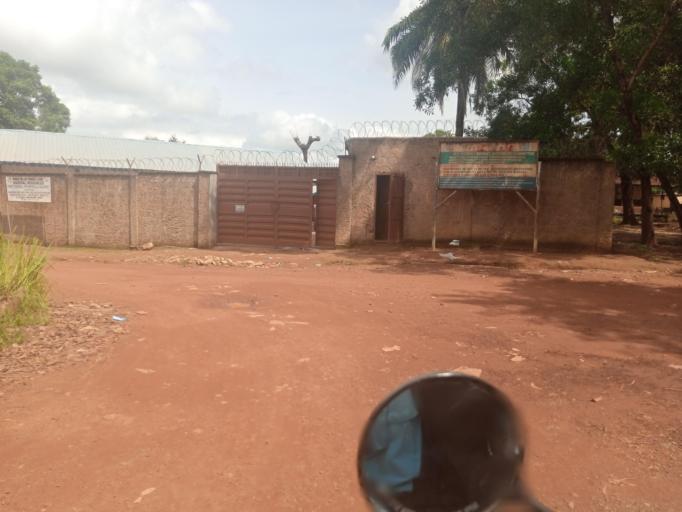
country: SL
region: Southern Province
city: Bo
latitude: 7.9681
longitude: -11.7429
